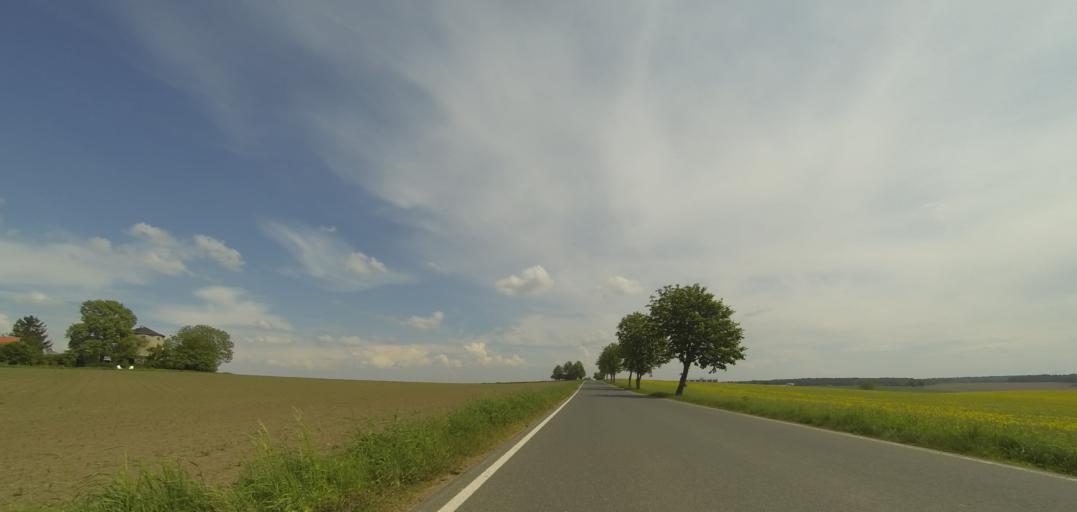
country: DE
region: Saxony
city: Radeberg
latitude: 51.0812
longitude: 13.9189
